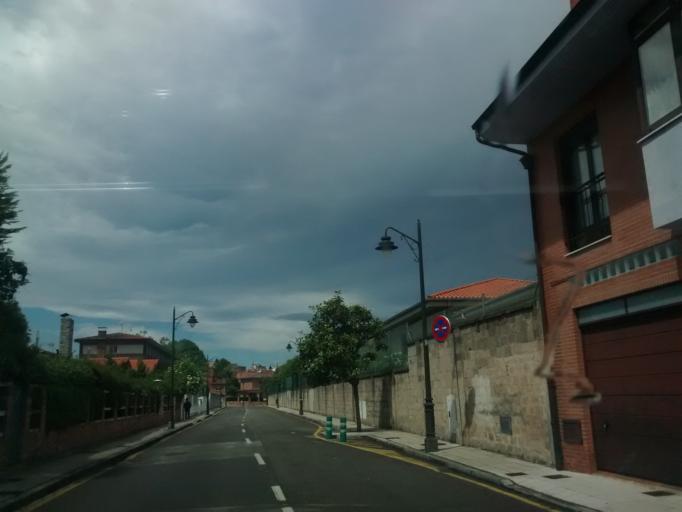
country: ES
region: Asturias
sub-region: Province of Asturias
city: Gijon
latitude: 43.5325
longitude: -5.6439
